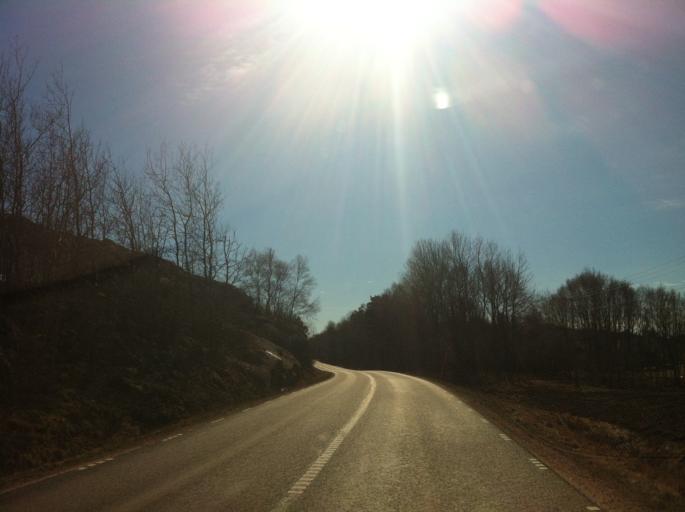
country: SE
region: Vaestra Goetaland
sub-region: Sotenas Kommun
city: Hunnebostrand
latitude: 58.4180
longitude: 11.3009
